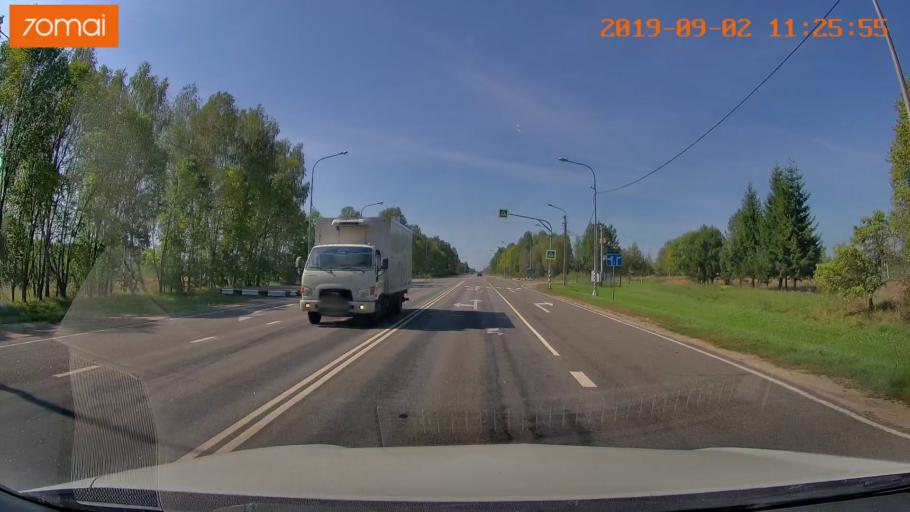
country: RU
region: Smolensk
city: Roslavl'
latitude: 53.9969
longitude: 32.9422
